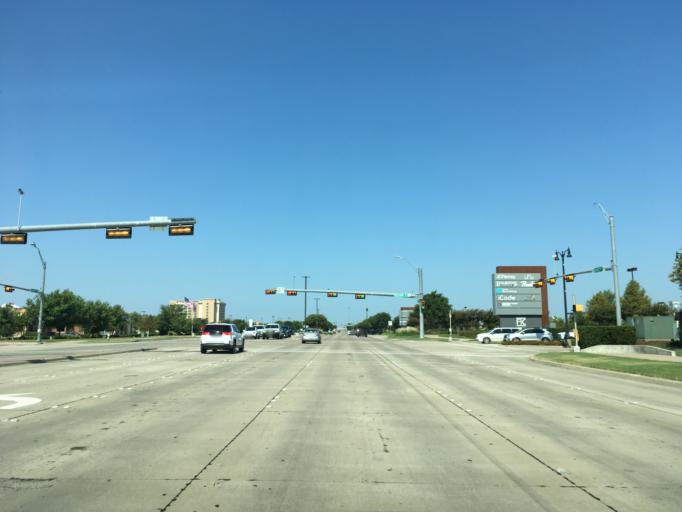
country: US
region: Texas
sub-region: Collin County
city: Fairview
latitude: 33.1298
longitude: -96.6482
